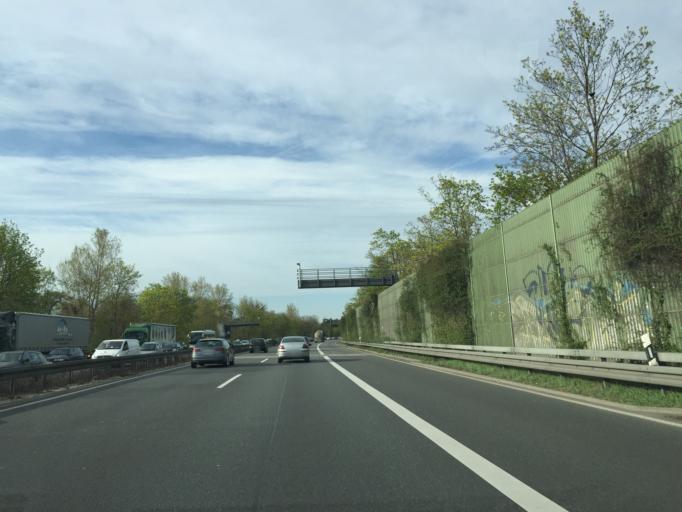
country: DE
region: Hesse
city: Pfungstadt
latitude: 49.8176
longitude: 8.6288
